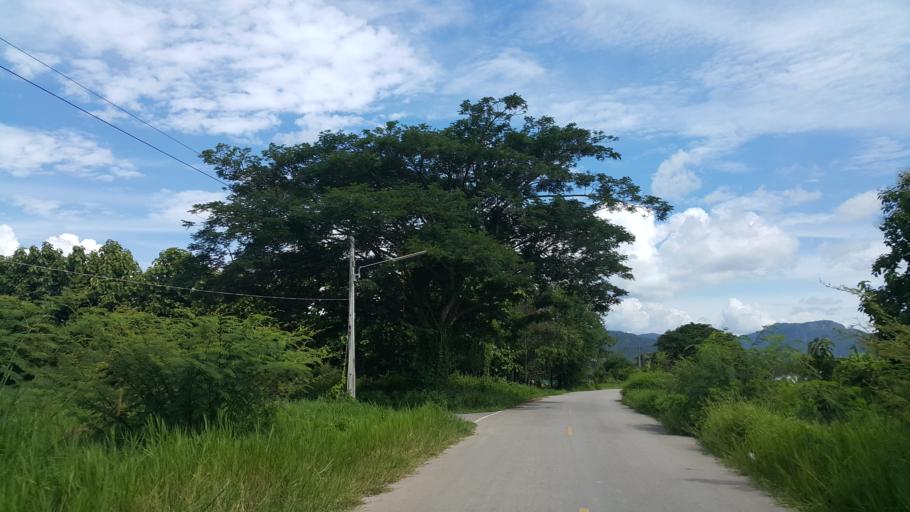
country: TH
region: Chiang Mai
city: Mae On
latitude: 18.7380
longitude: 99.2028
